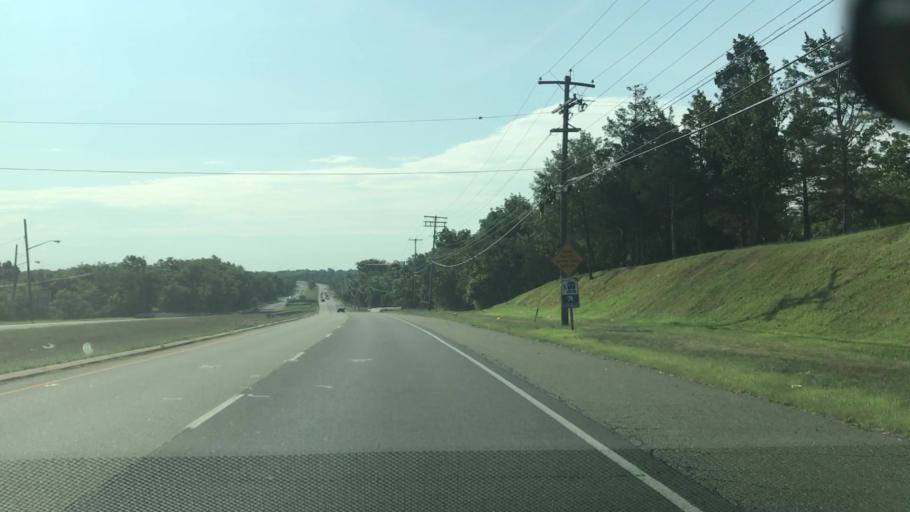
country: US
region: New Jersey
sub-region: Somerset County
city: Bridgewater
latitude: 40.5985
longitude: -74.6810
